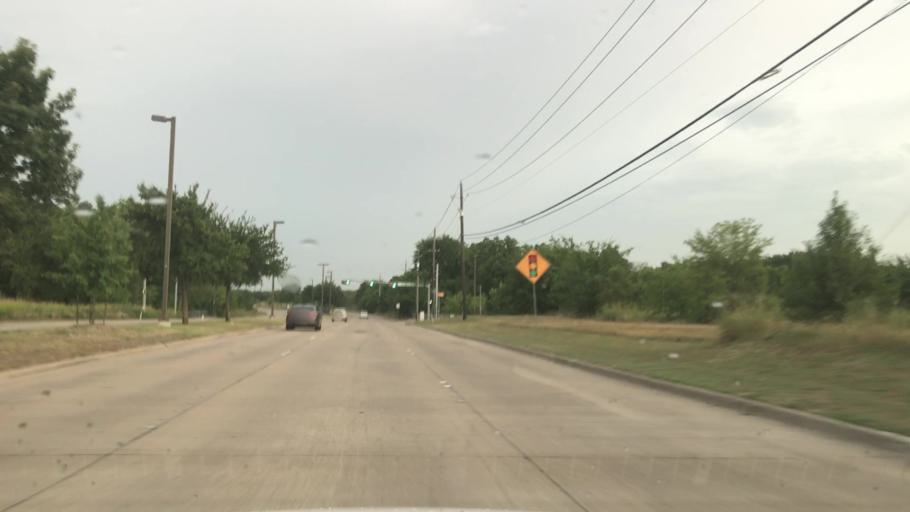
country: US
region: Texas
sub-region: Dallas County
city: Mesquite
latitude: 32.7393
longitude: -96.5738
